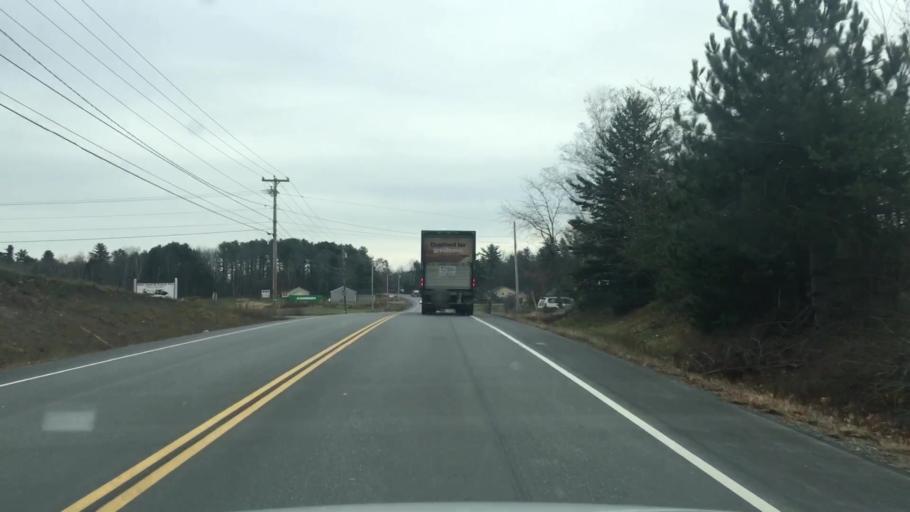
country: US
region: Maine
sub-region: Waldo County
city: Belfast
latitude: 44.4141
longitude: -69.0546
